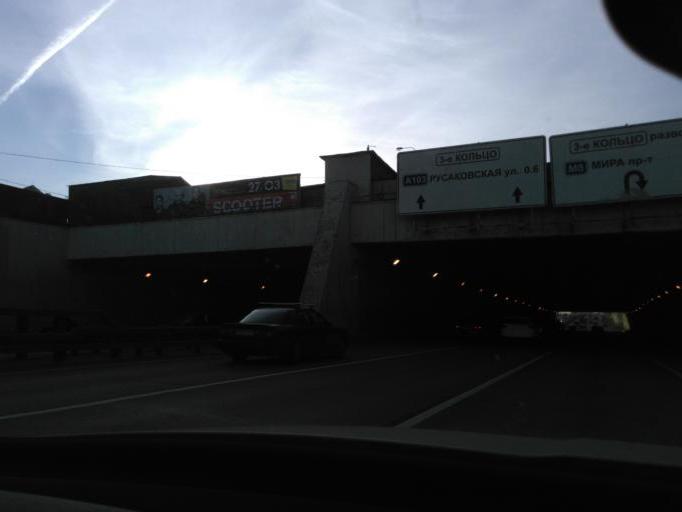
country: RU
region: Moscow
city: Sokol'niki
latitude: 55.7881
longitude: 37.6598
